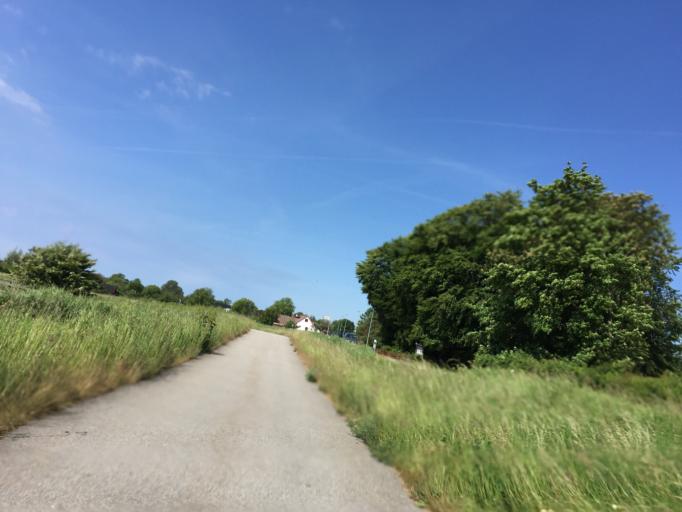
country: SE
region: Skane
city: Smygehamn
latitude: 55.3436
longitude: 13.3235
